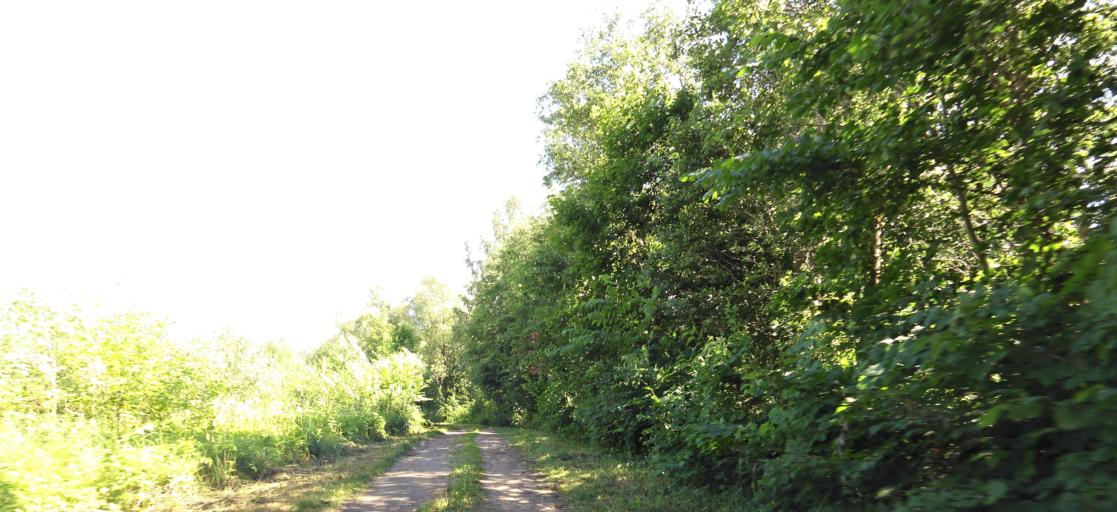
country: LT
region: Panevezys
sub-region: Birzai
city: Birzai
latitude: 56.3834
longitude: 24.7023
